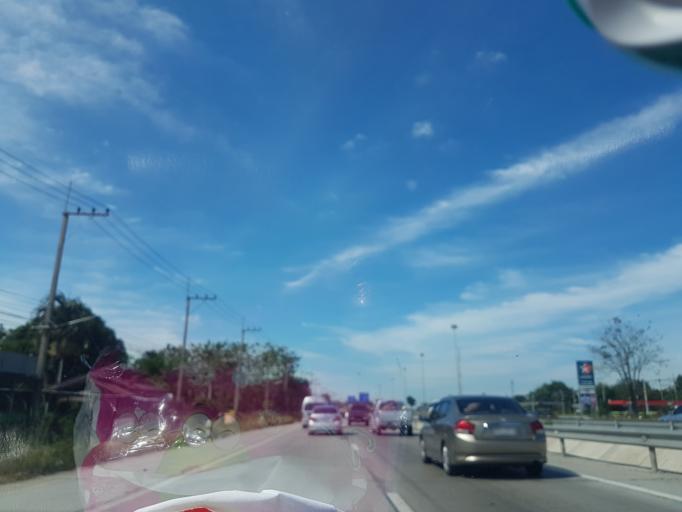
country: TH
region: Chon Buri
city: Bang Lamung
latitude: 12.9590
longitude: 100.9841
